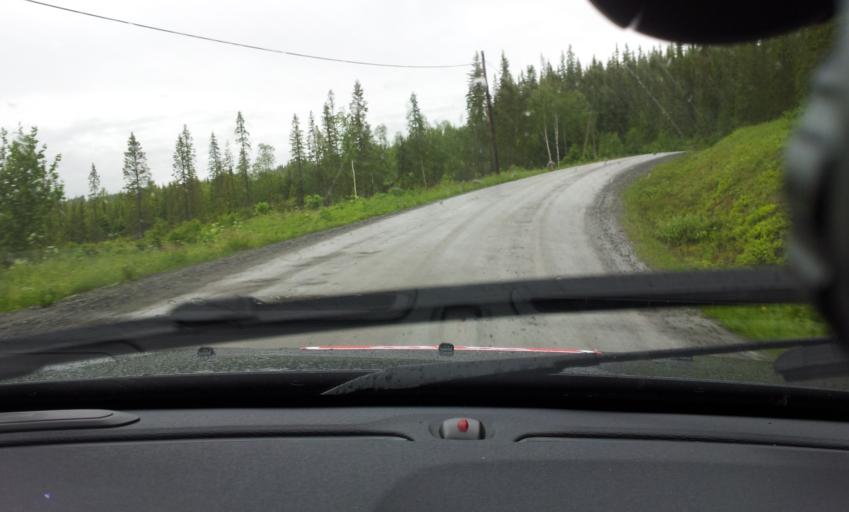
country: SE
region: Jaemtland
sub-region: Are Kommun
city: Are
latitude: 63.4196
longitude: 12.8238
